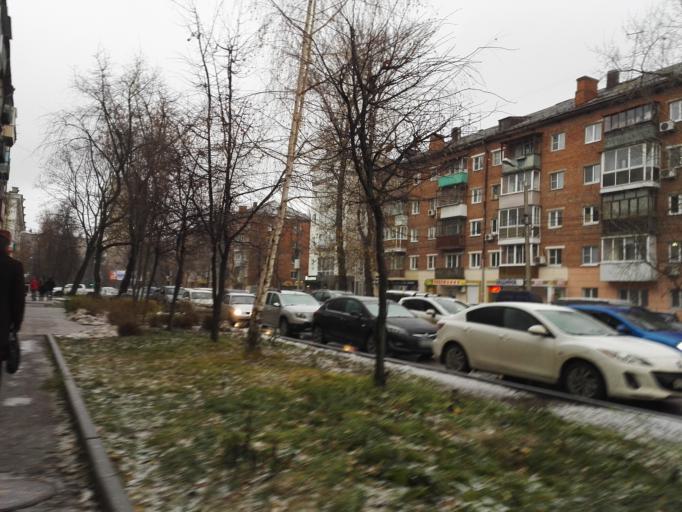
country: RU
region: Tula
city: Tula
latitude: 54.1737
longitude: 37.5954
